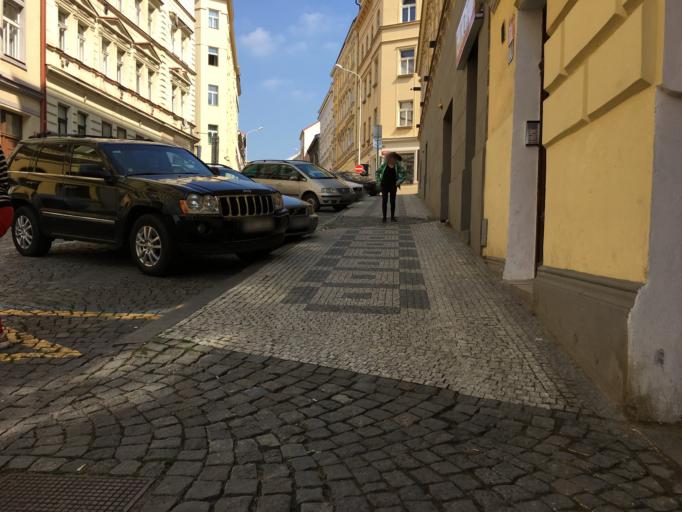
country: CZ
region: Praha
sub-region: Praha 8
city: Karlin
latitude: 50.0854
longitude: 14.4491
